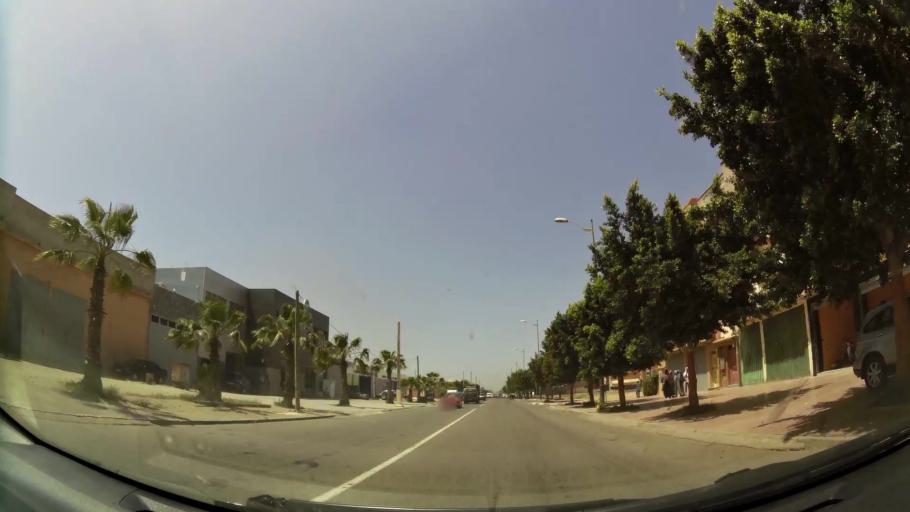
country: MA
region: Souss-Massa-Draa
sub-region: Inezgane-Ait Mellou
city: Inezgane
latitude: 30.3407
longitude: -9.4840
